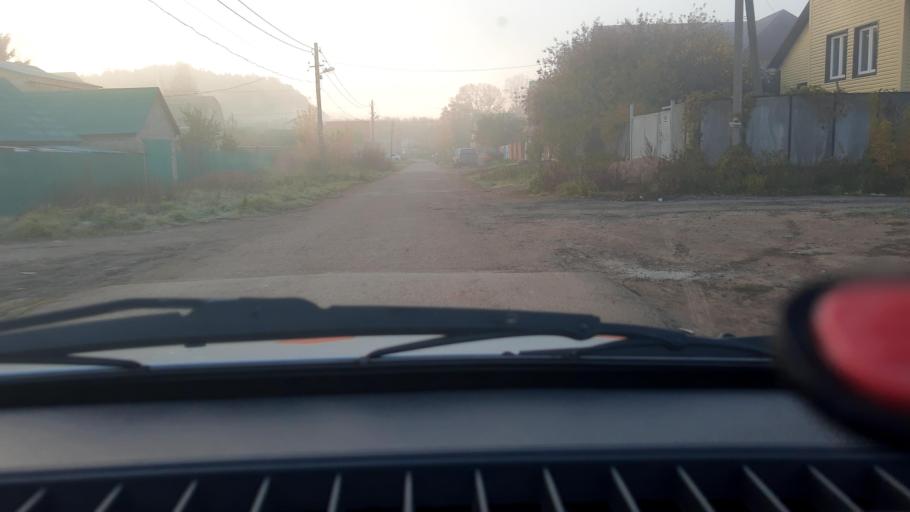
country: RU
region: Bashkortostan
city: Ufa
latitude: 54.7297
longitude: 55.9057
